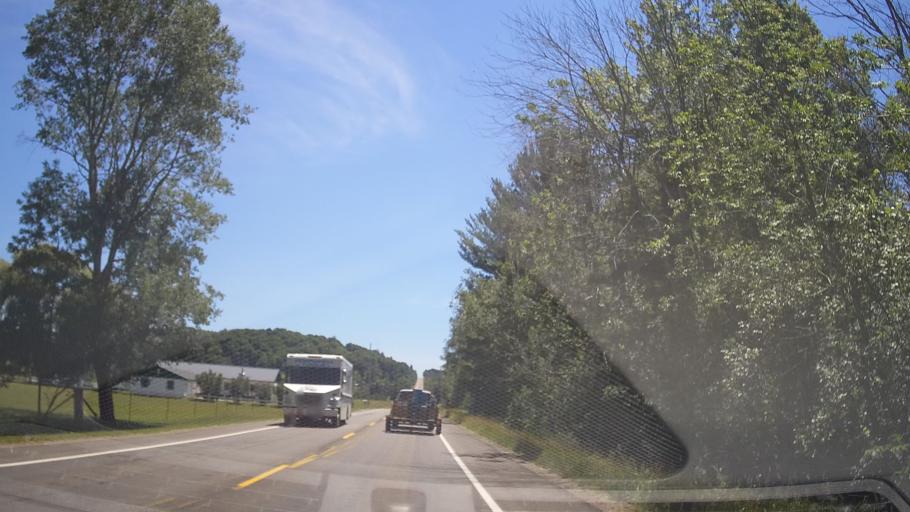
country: US
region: Michigan
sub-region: Grand Traverse County
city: Traverse City
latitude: 44.6326
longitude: -85.6964
